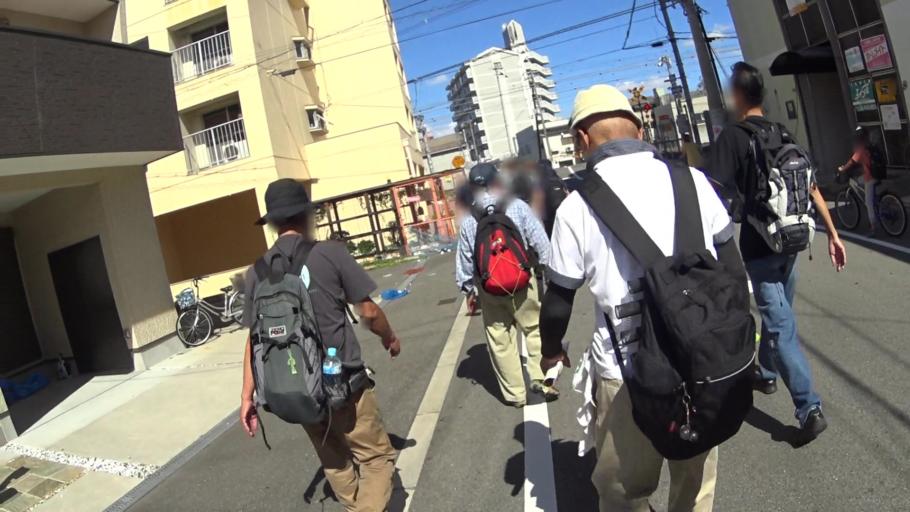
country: JP
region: Osaka
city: Yao
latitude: 34.6291
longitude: 135.5564
